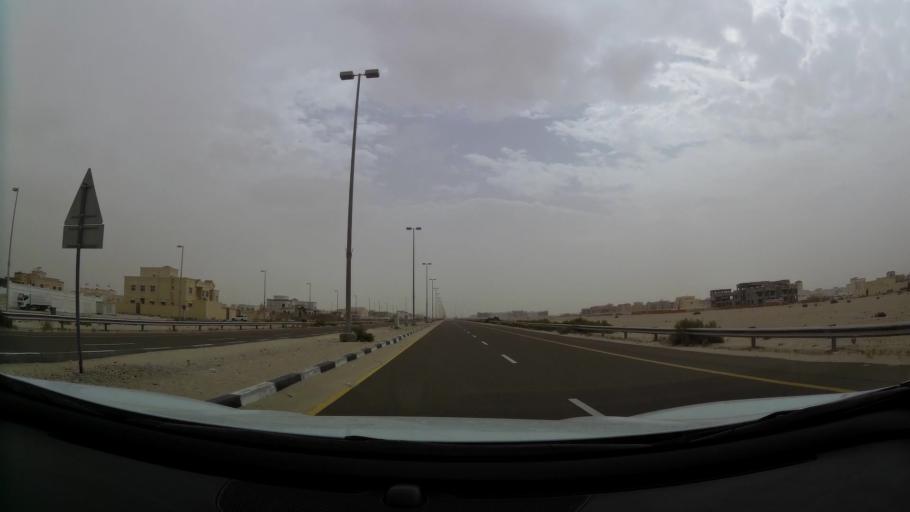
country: AE
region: Abu Dhabi
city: Abu Dhabi
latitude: 24.3632
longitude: 54.6968
